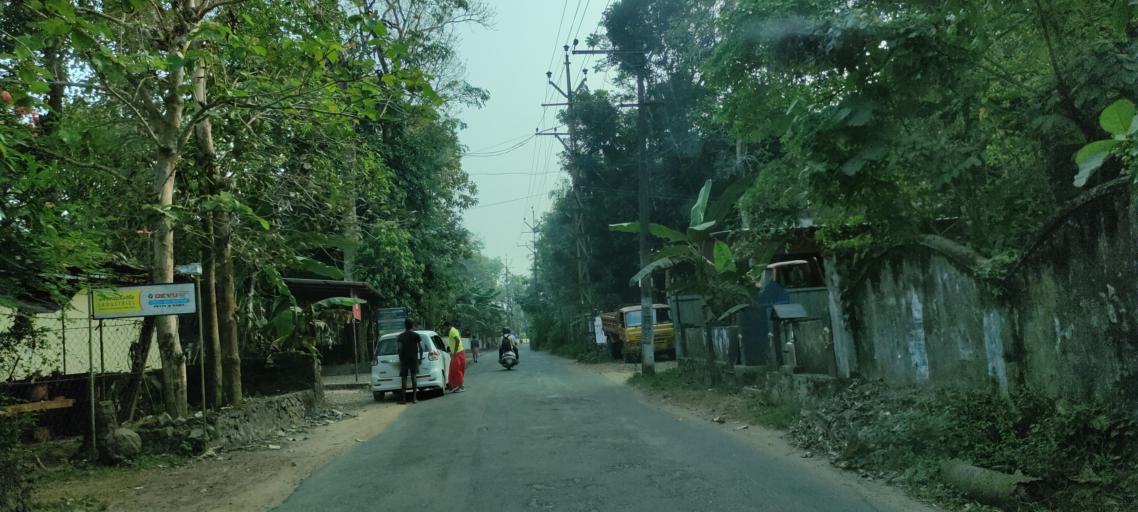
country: IN
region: Kerala
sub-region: Kottayam
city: Vaikam
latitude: 9.7272
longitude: 76.4767
